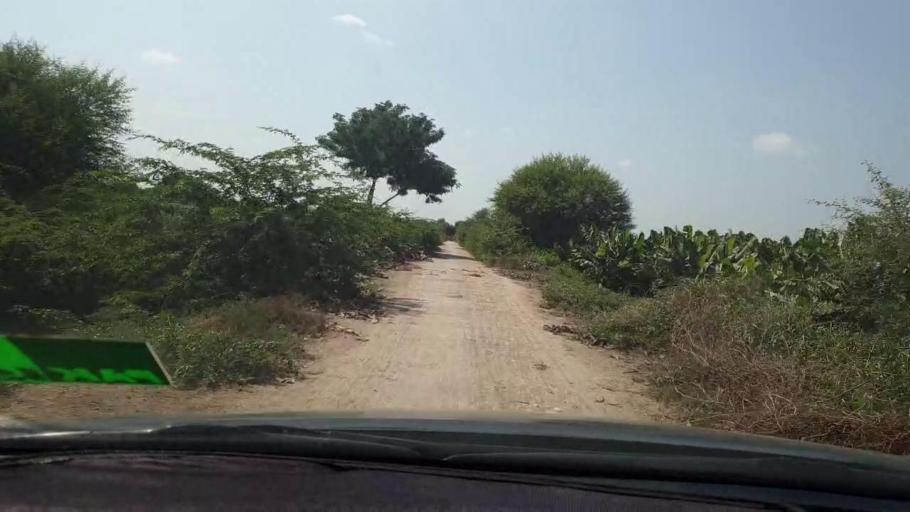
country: PK
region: Sindh
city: Naukot
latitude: 24.9149
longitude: 69.2425
